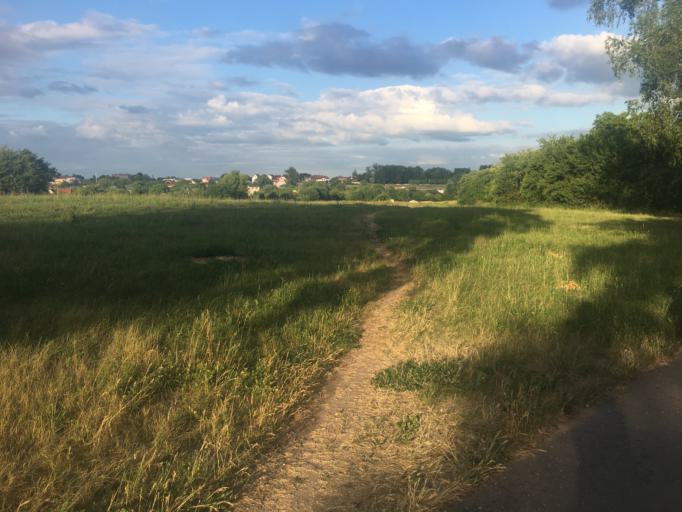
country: BY
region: Grodnenskaya
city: Hrodna
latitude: 53.6836
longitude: 23.8068
